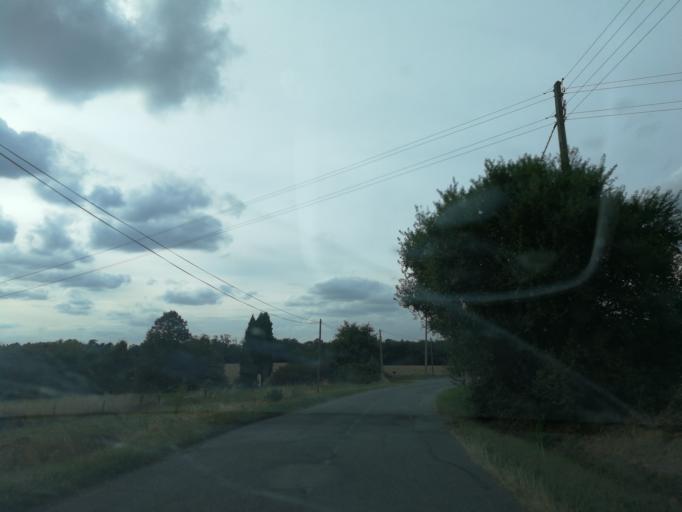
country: FR
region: Midi-Pyrenees
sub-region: Departement de la Haute-Garonne
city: Flourens
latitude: 43.6037
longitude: 1.5376
